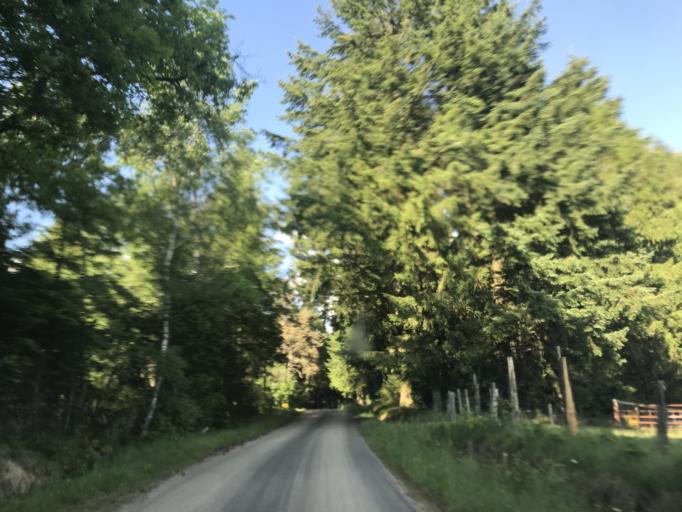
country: FR
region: Auvergne
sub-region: Departement du Puy-de-Dome
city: Job
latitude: 45.6776
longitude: 3.6835
